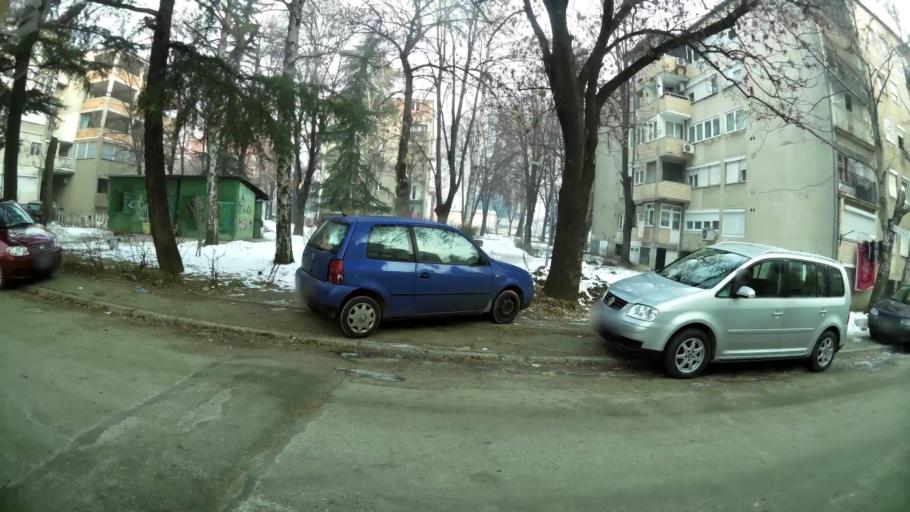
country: MK
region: Cair
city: Cair
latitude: 42.0195
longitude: 21.4457
